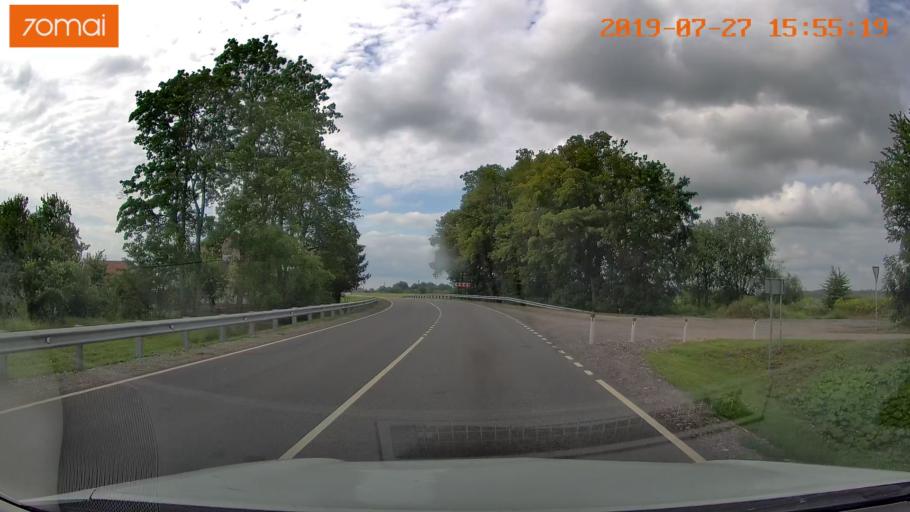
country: RU
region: Kaliningrad
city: Chernyakhovsk
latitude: 54.6133
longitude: 21.9226
